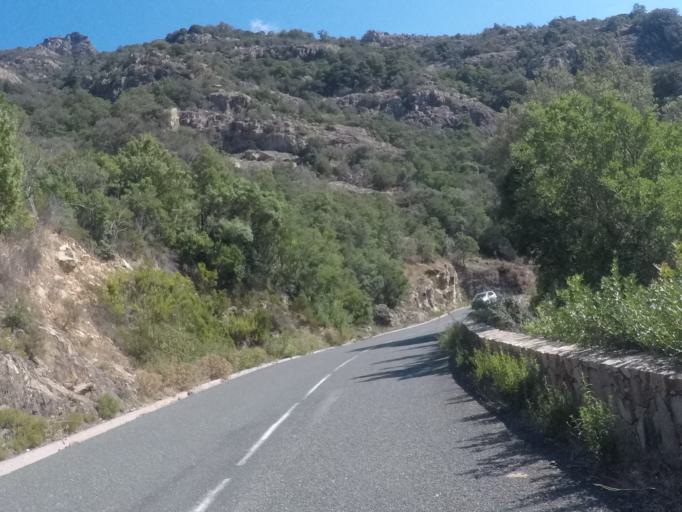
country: FR
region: Corsica
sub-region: Departement de la Haute-Corse
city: Calvi
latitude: 42.3839
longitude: 8.6985
